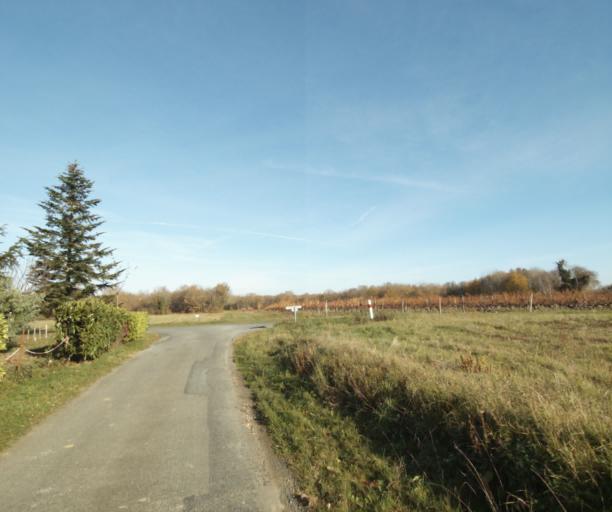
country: FR
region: Poitou-Charentes
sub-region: Departement de la Charente-Maritime
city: Cherac
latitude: 45.7428
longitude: -0.4662
